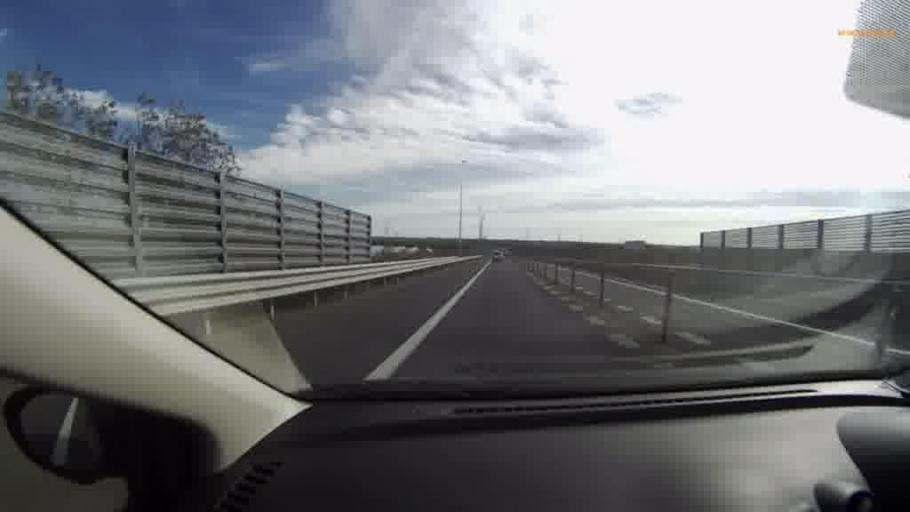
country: JP
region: Hokkaido
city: Kushiro
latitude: 43.0332
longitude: 144.3876
